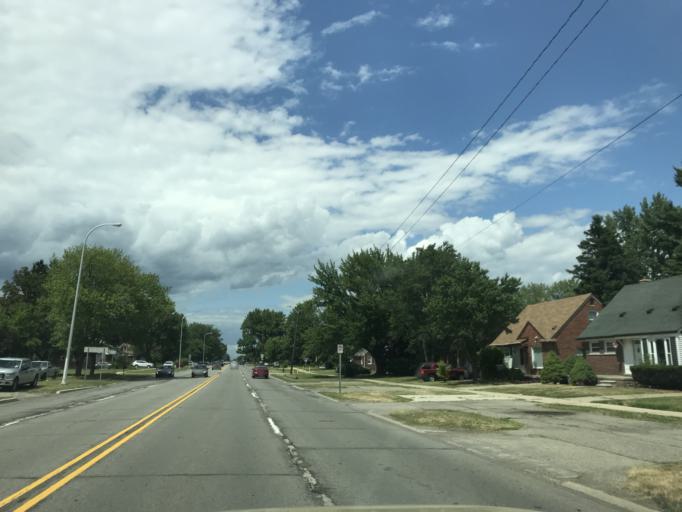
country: US
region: Michigan
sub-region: Wayne County
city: Redford
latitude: 42.3640
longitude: -83.3132
